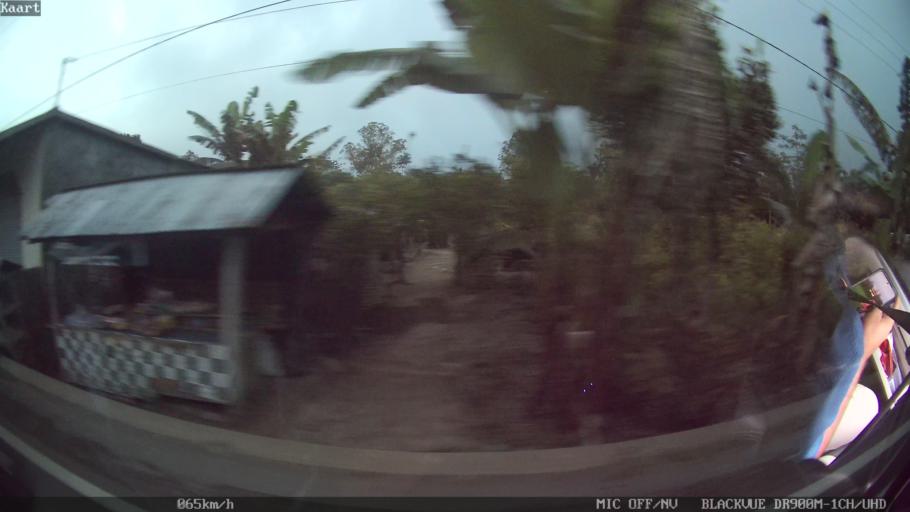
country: ID
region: Bali
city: Banjar Kedisan
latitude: -8.2819
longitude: 115.3218
